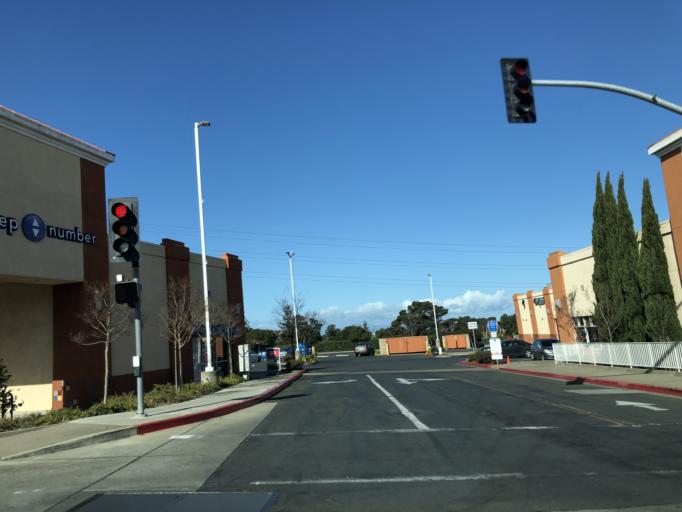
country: US
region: California
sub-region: Contra Costa County
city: Tara Hills
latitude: 37.9909
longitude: -122.3067
